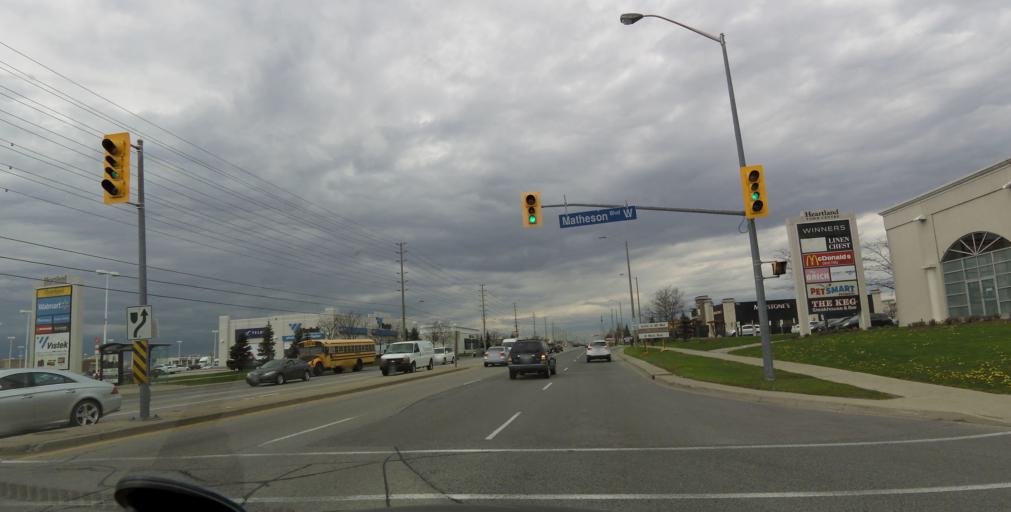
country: CA
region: Ontario
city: Mississauga
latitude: 43.6082
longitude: -79.6904
